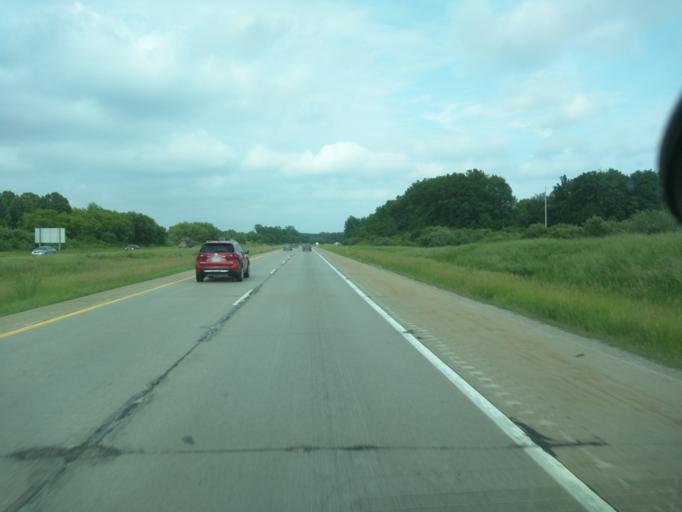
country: US
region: Michigan
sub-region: Clinton County
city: Bath
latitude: 42.8027
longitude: -84.4804
